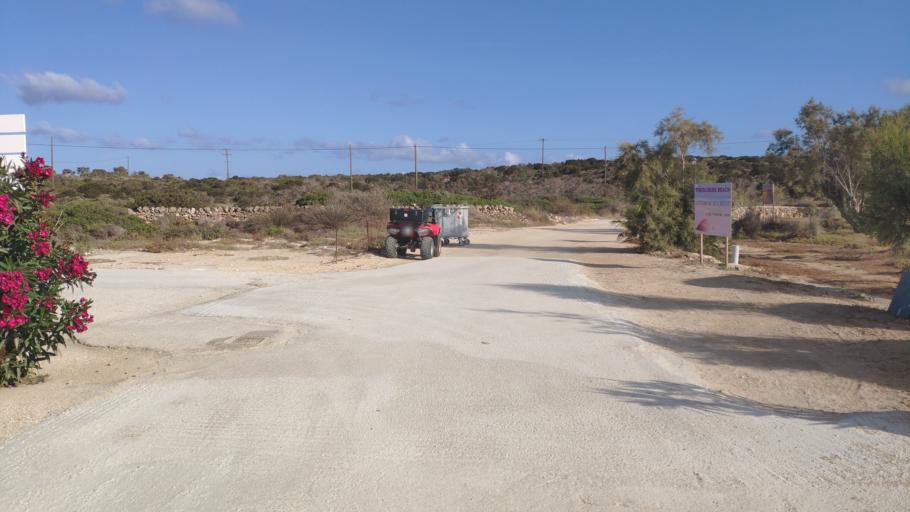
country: GR
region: South Aegean
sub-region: Nomos Kykladon
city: Antiparos
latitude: 37.0436
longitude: 25.0851
